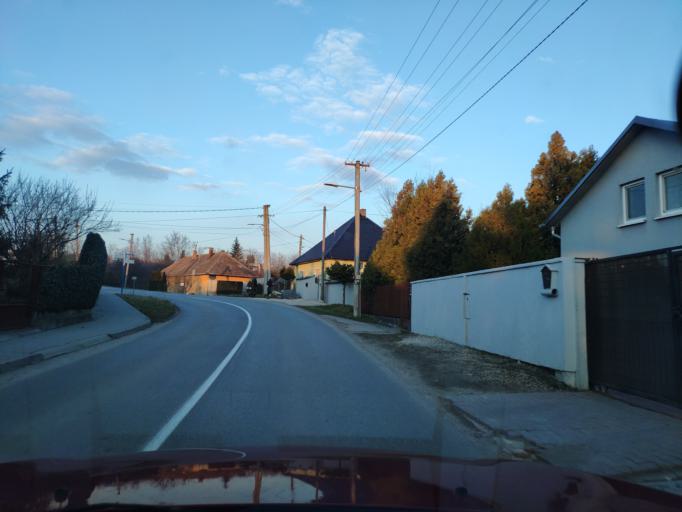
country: SK
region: Nitriansky
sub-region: Okres Nitra
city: Nitra
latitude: 48.2099
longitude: 18.0701
